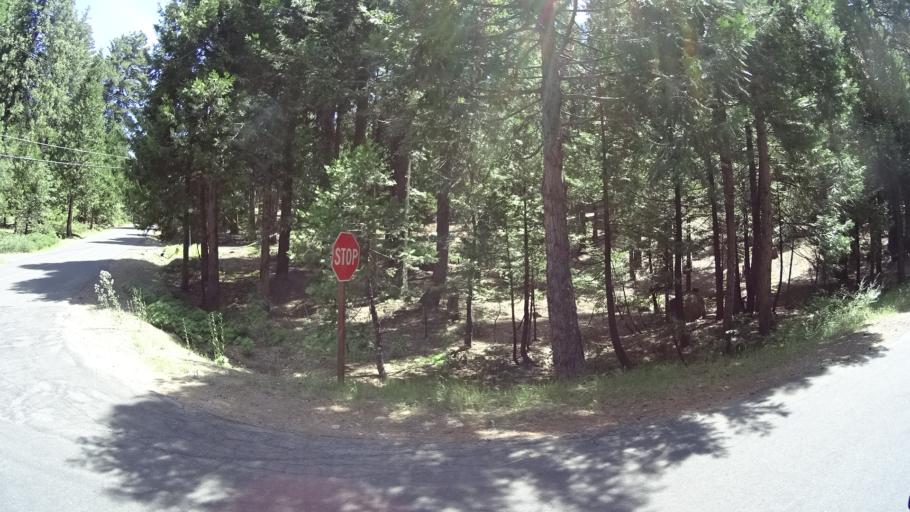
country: US
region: California
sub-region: Calaveras County
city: Arnold
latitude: 38.3102
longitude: -120.2623
